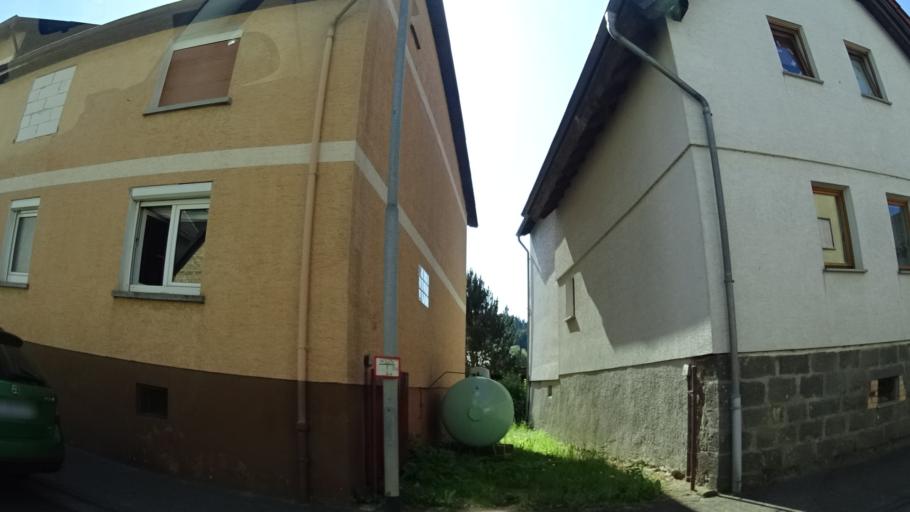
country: DE
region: Hesse
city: Beuern
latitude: 50.6312
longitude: 8.8266
